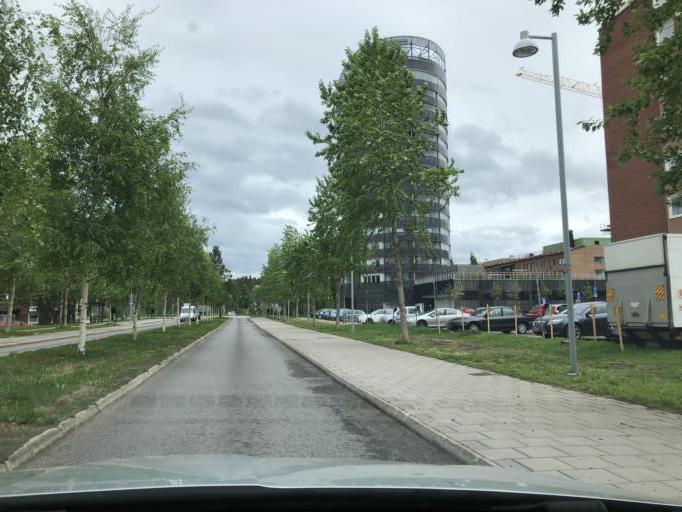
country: SE
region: Norrbotten
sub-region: Pitea Kommun
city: Pitea
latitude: 65.3163
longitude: 21.4875
